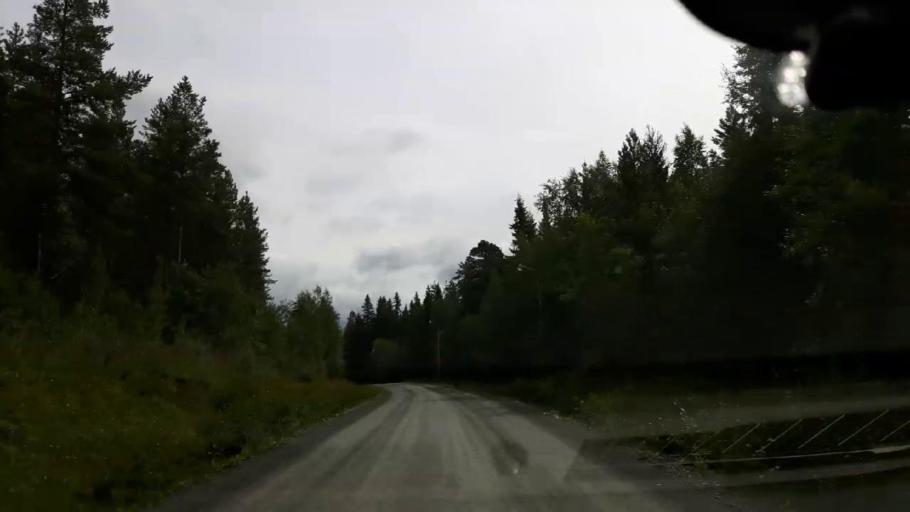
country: SE
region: Jaemtland
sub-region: Krokoms Kommun
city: Valla
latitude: 63.6291
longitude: 14.0216
